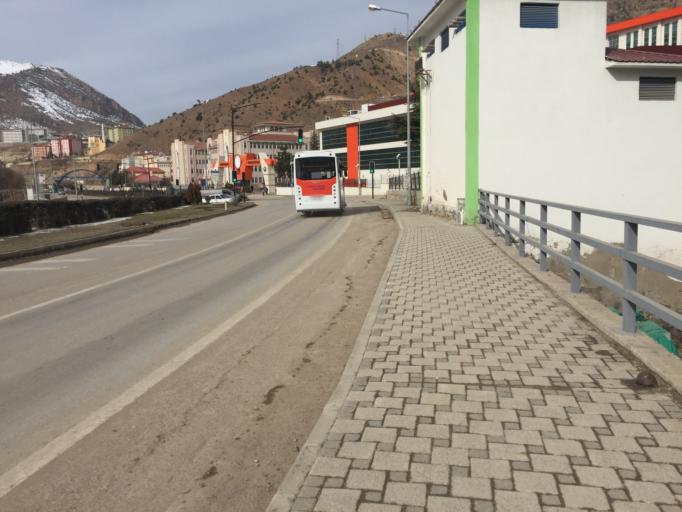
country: TR
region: Gumushane
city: Gumushkhane
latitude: 40.4346
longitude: 39.5177
